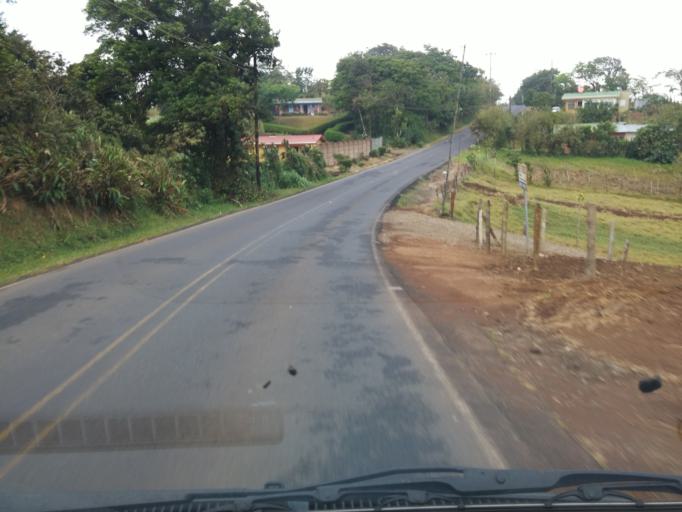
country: CR
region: Alajuela
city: San Ramon
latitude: 10.1413
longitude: -84.4816
